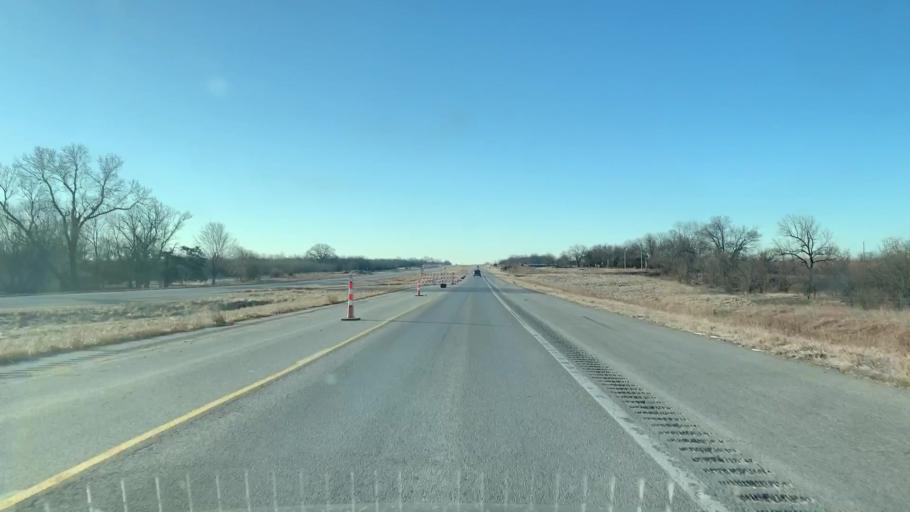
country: US
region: Kansas
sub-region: Bourbon County
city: Fort Scott
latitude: 37.7637
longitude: -94.7049
